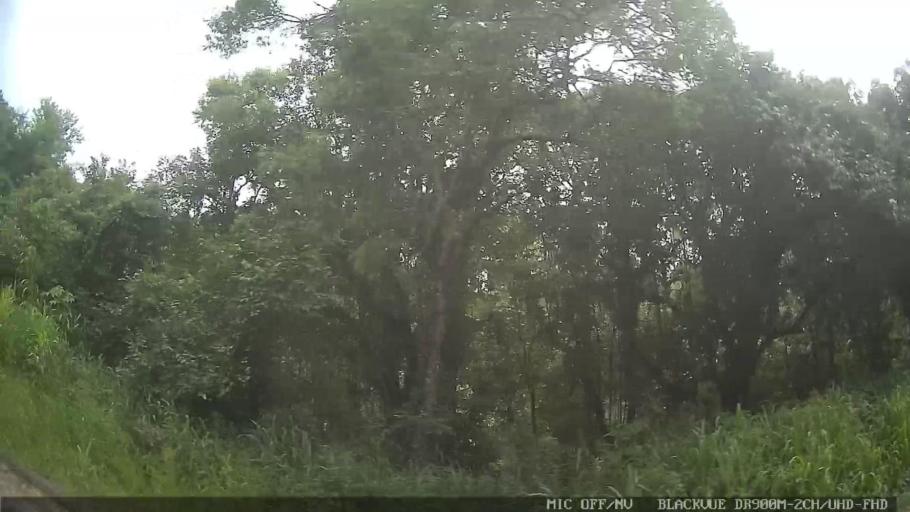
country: BR
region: Sao Paulo
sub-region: Aruja
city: Aruja
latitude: -23.4179
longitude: -46.2684
